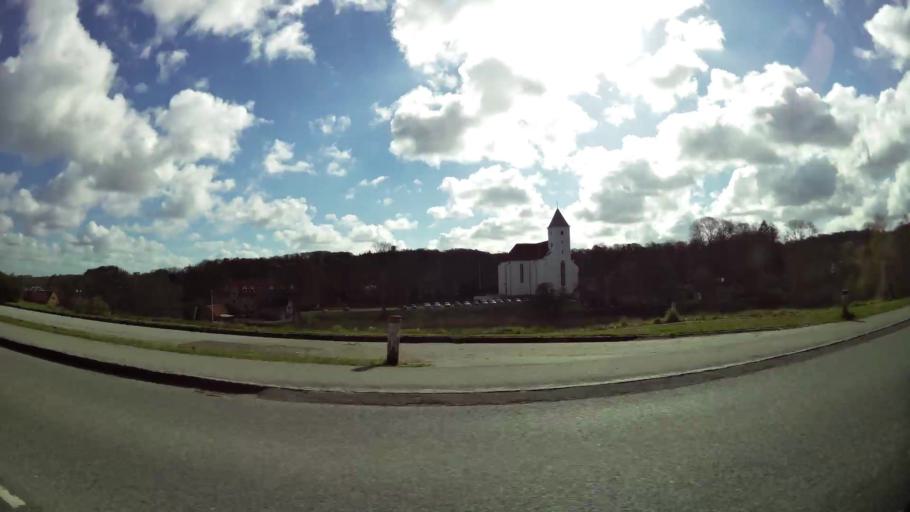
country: DK
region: North Denmark
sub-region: Mariagerfjord Kommune
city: Mariager
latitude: 56.6484
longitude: 9.9758
